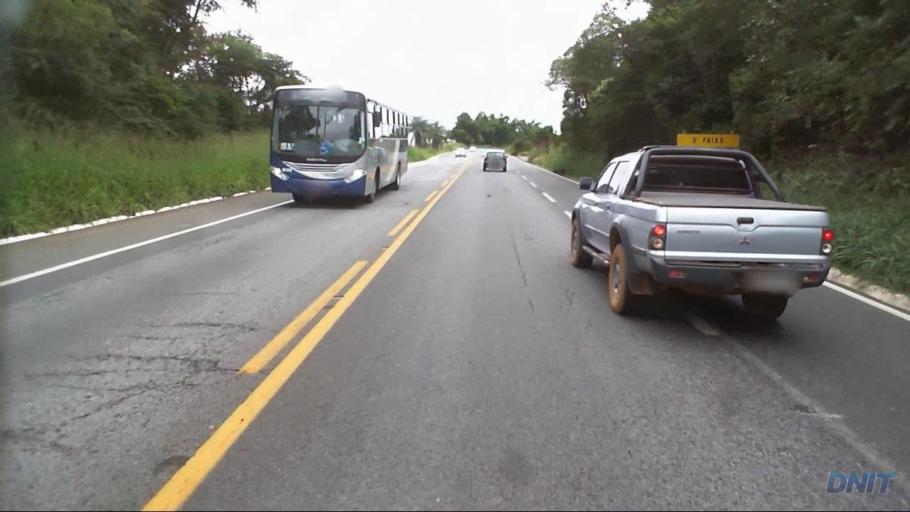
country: BR
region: Minas Gerais
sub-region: Joao Monlevade
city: Joao Monlevade
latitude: -19.8509
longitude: -43.2994
